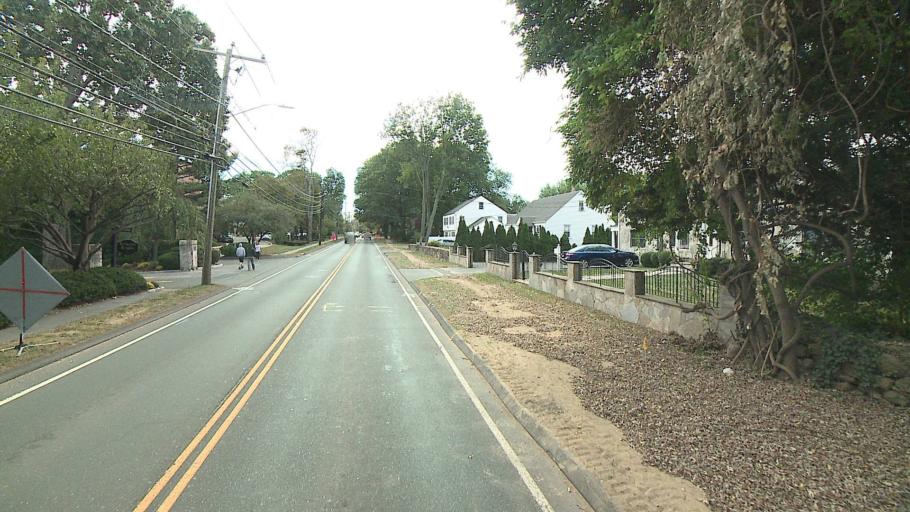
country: US
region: Connecticut
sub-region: Fairfield County
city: Stamford
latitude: 41.0615
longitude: -73.5143
